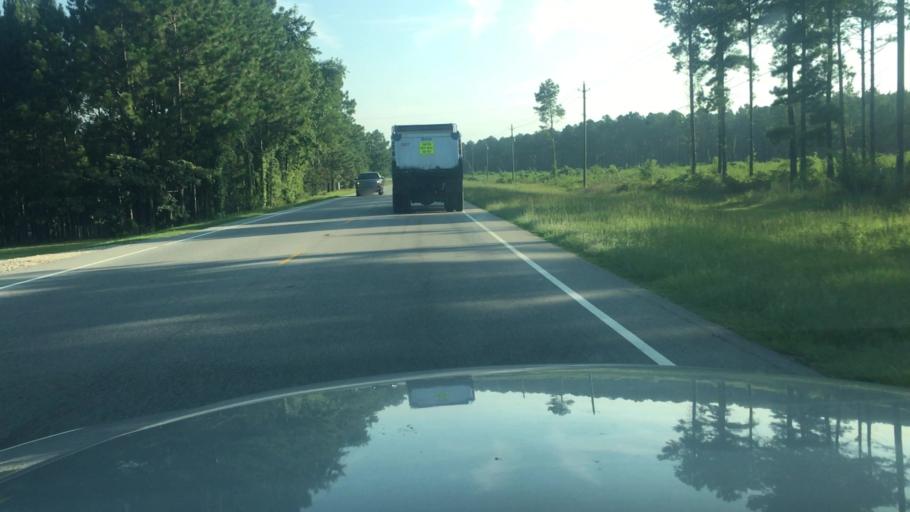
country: US
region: North Carolina
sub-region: Harnett County
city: Walkertown
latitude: 35.1900
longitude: -78.8510
